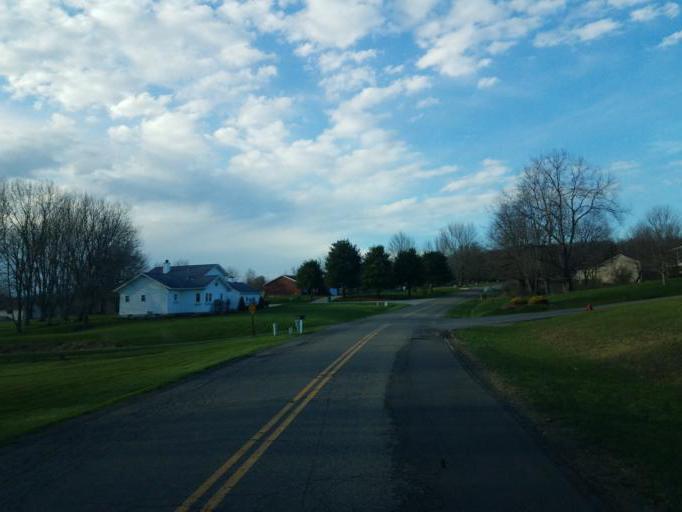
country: US
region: Ohio
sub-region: Knox County
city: Gambier
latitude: 40.4239
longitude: -82.3433
